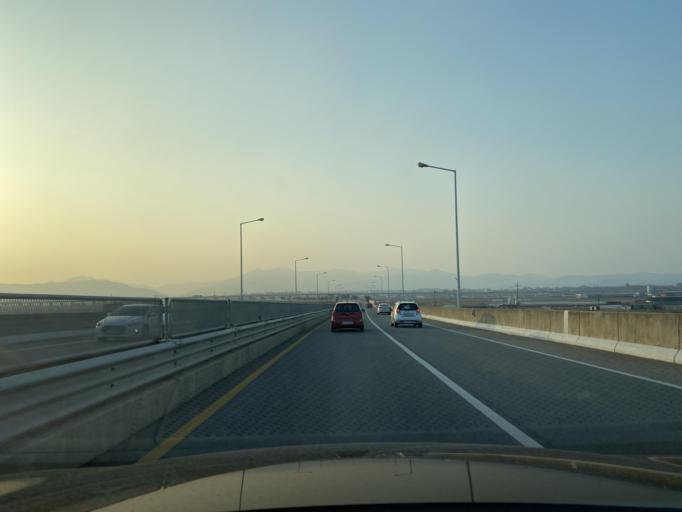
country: KR
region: Chungcheongnam-do
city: Yesan
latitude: 36.6908
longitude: 126.7377
